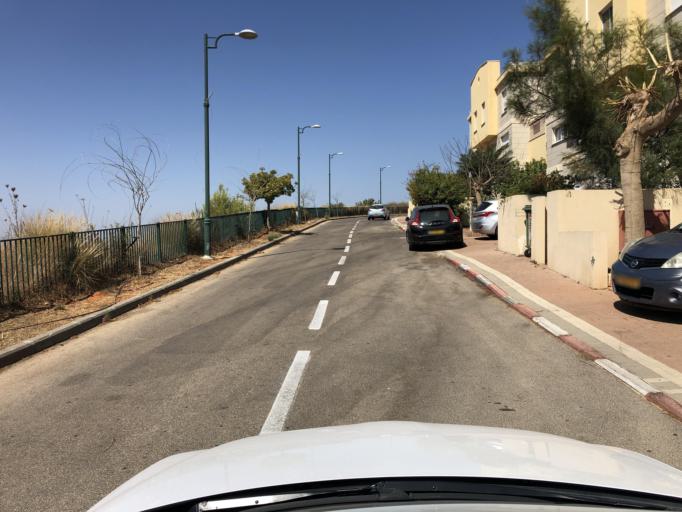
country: PS
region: West Bank
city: An Nabi Ilyas
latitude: 32.1663
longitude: 35.0170
